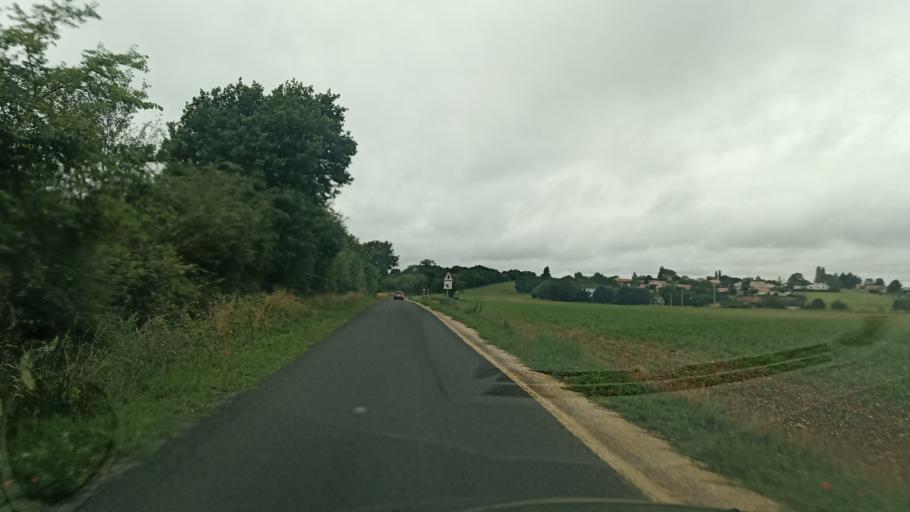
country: FR
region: Poitou-Charentes
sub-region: Departement de la Vienne
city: Biard
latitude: 46.5925
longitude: 0.2882
